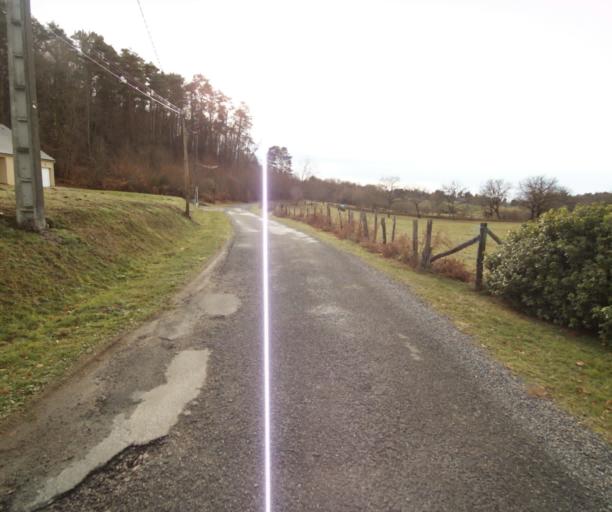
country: FR
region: Limousin
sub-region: Departement de la Correze
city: Saint-Mexant
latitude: 45.2787
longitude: 1.6794
